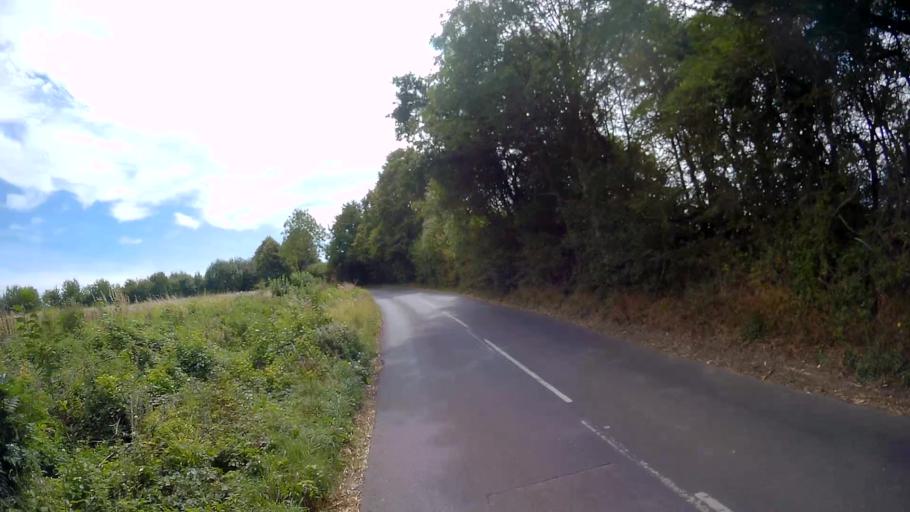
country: GB
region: England
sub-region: Hampshire
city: Long Sutton
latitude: 51.2278
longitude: -0.9575
